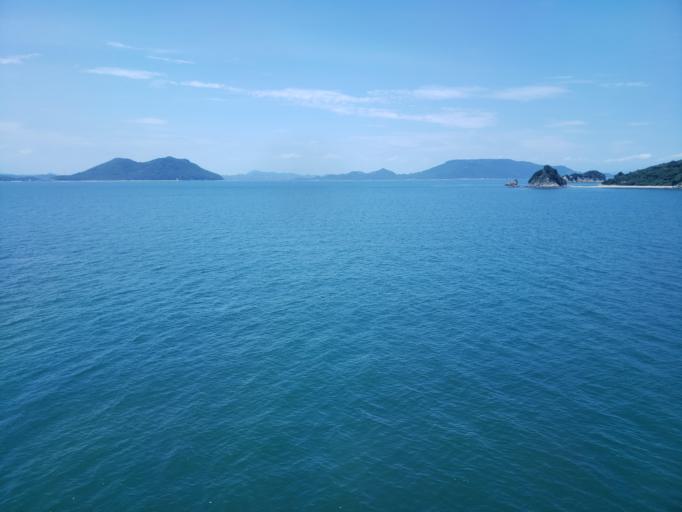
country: JP
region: Kagawa
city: Takamatsu-shi
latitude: 34.3939
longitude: 134.0992
